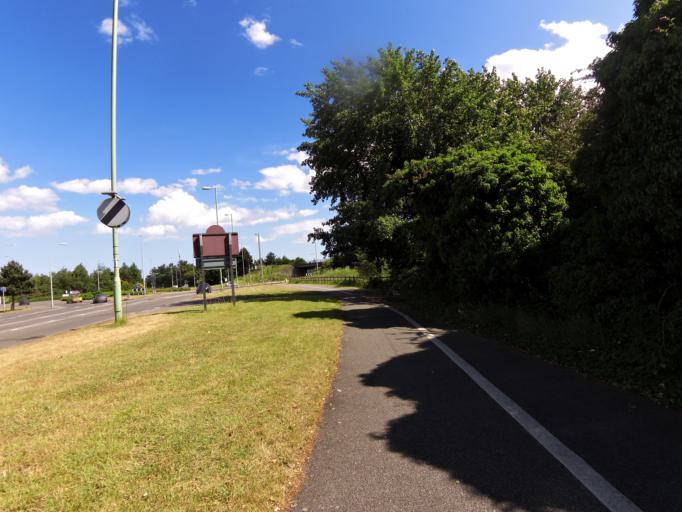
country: GB
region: England
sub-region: Suffolk
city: Kesgrave
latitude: 52.0264
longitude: 1.2063
